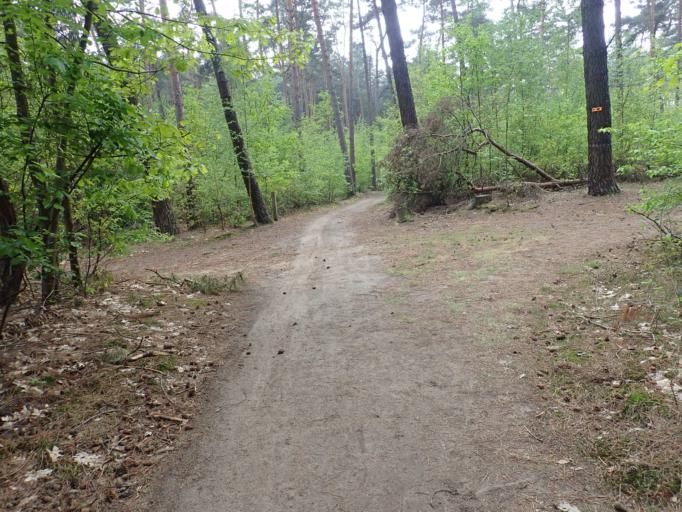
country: BE
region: Flanders
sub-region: Provincie Antwerpen
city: Herentals
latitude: 51.1983
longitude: 4.8489
